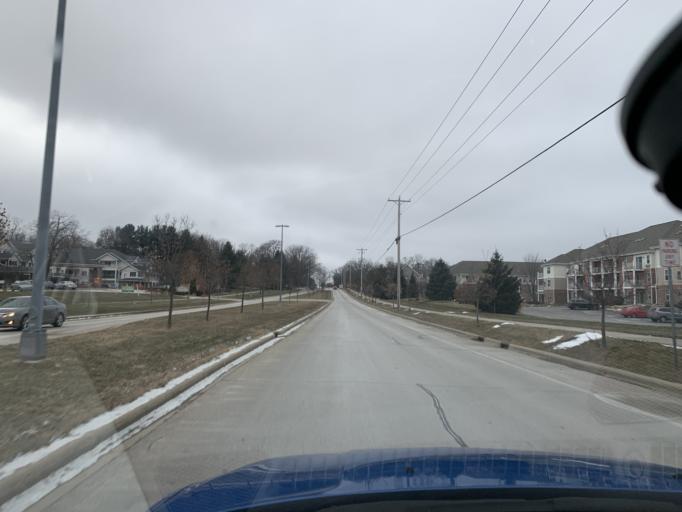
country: US
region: Wisconsin
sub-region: Dane County
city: Middleton
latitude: 43.0749
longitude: -89.5489
